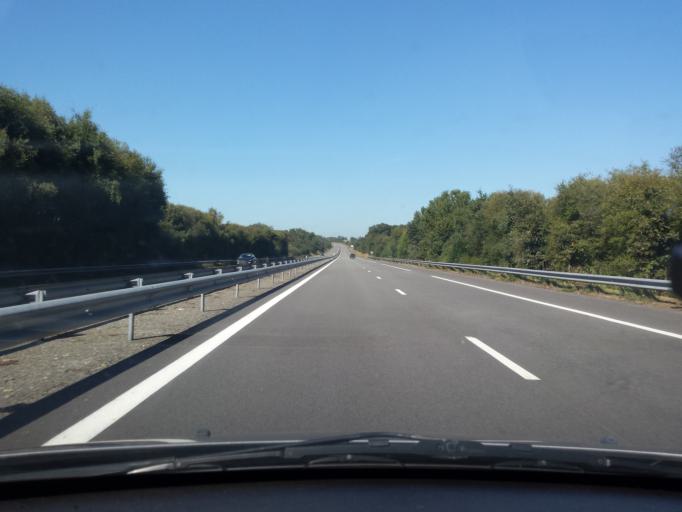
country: FR
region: Brittany
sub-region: Departement du Morbihan
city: Naizin
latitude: 47.9884
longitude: -2.8755
